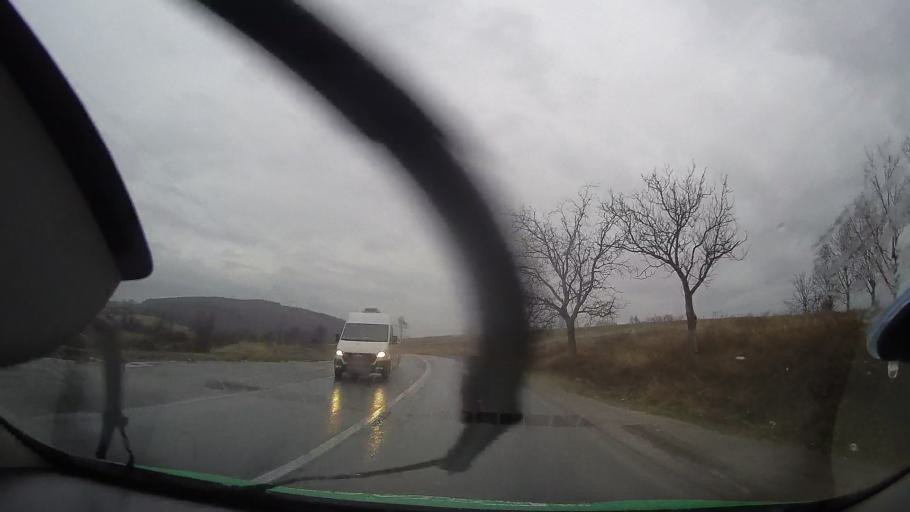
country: RO
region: Bihor
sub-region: Comuna Rabagani
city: Rabagani
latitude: 46.7271
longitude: 22.2406
